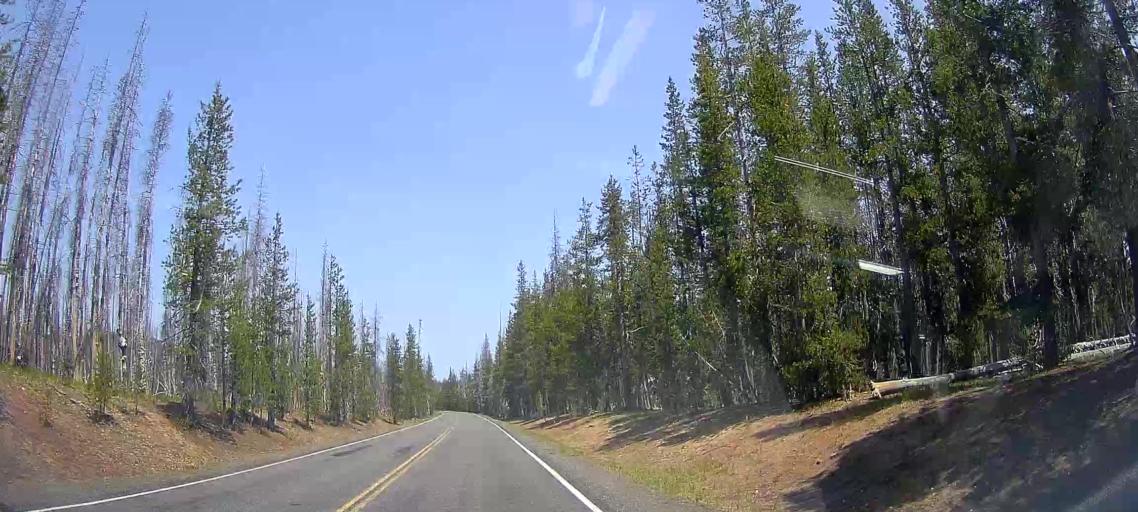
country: US
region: Oregon
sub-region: Lane County
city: Oakridge
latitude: 43.0409
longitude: -122.1174
